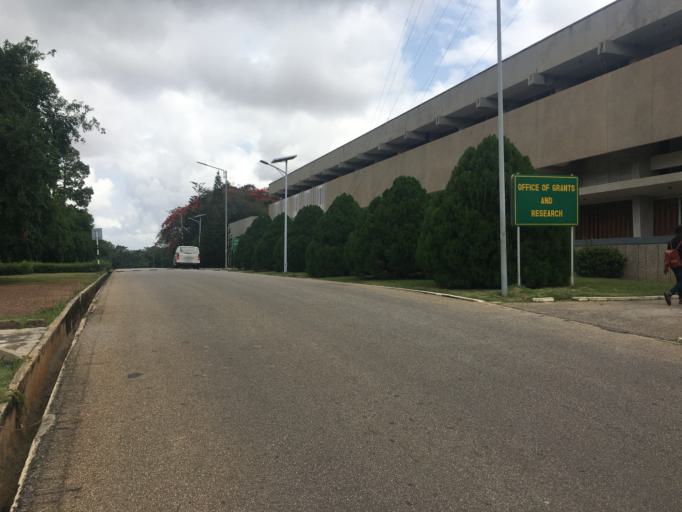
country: GH
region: Ashanti
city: Kumasi
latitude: 6.6744
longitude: -1.5729
